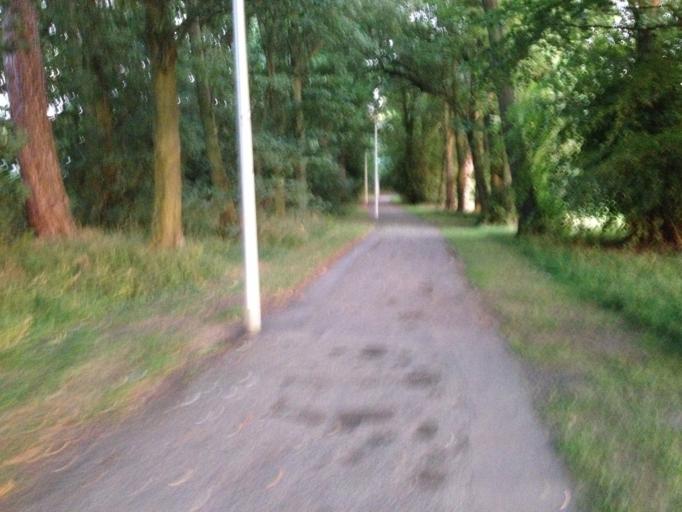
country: GB
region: Scotland
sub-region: West Lothian
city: Livingston
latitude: 55.8898
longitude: -3.5121
